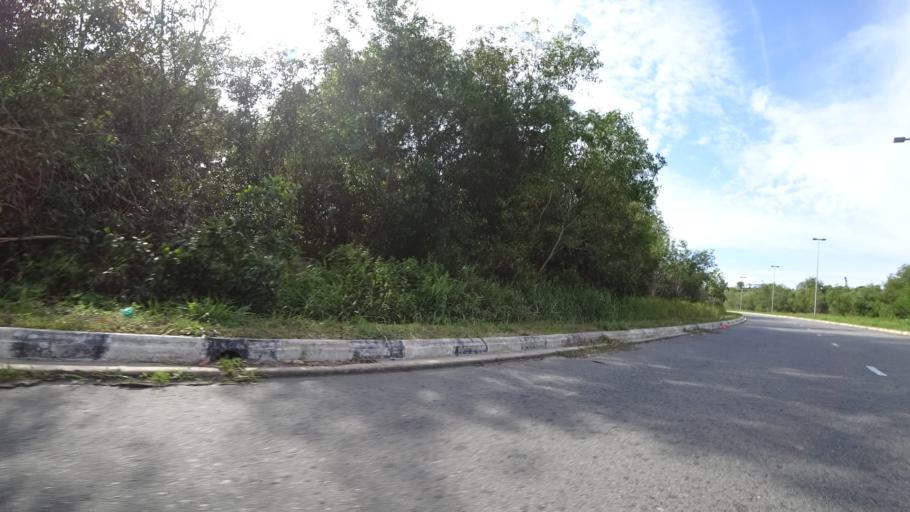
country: BN
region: Brunei and Muara
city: Bandar Seri Begawan
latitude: 4.8982
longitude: 114.8030
